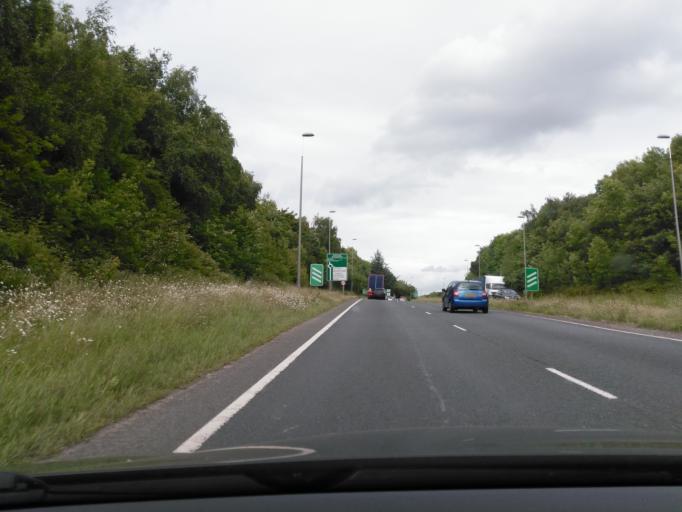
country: GB
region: England
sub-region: Hampshire
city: Basingstoke
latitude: 51.2850
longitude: -1.0662
